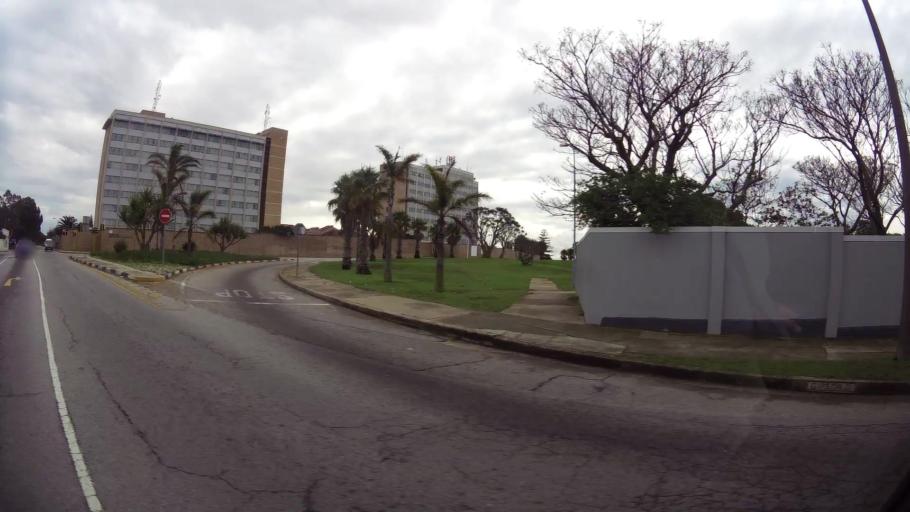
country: ZA
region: Eastern Cape
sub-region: Nelson Mandela Bay Metropolitan Municipality
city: Port Elizabeth
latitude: -33.9565
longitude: 25.5957
